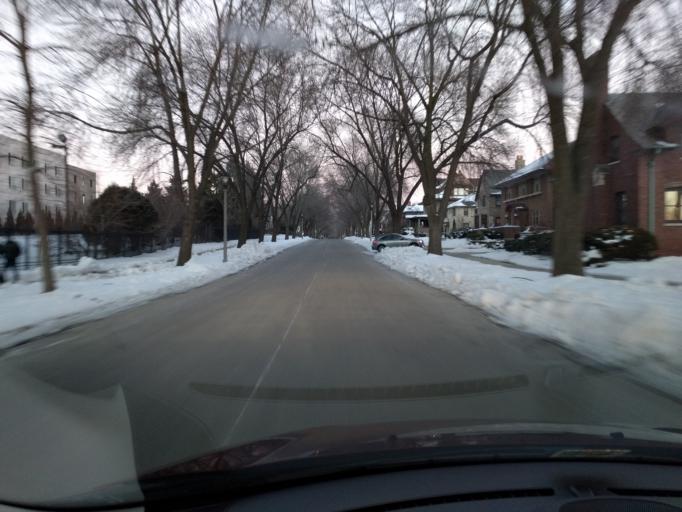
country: US
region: Wisconsin
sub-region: Milwaukee County
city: Shorewood
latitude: 43.0606
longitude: -87.8782
